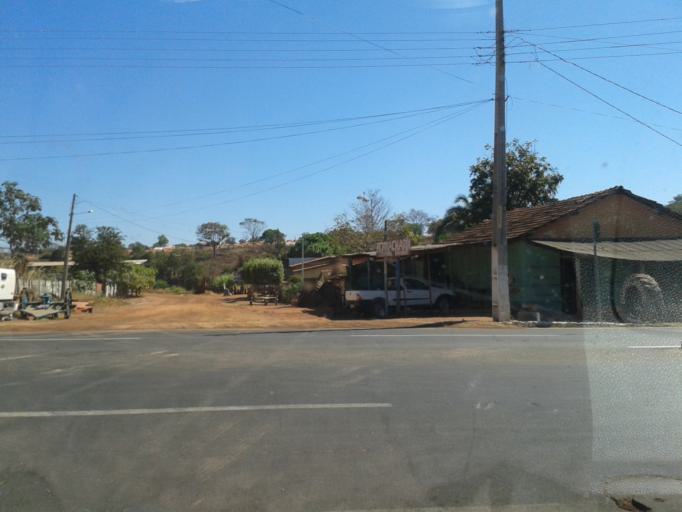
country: BR
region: Goias
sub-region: Sao Miguel Do Araguaia
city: Sao Miguel do Araguaia
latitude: -13.2704
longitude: -50.1597
